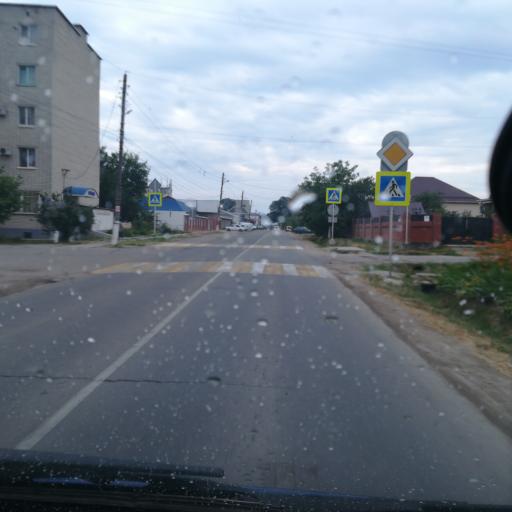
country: RU
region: Krasnodarskiy
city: Krymsk
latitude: 44.9349
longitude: 37.9816
